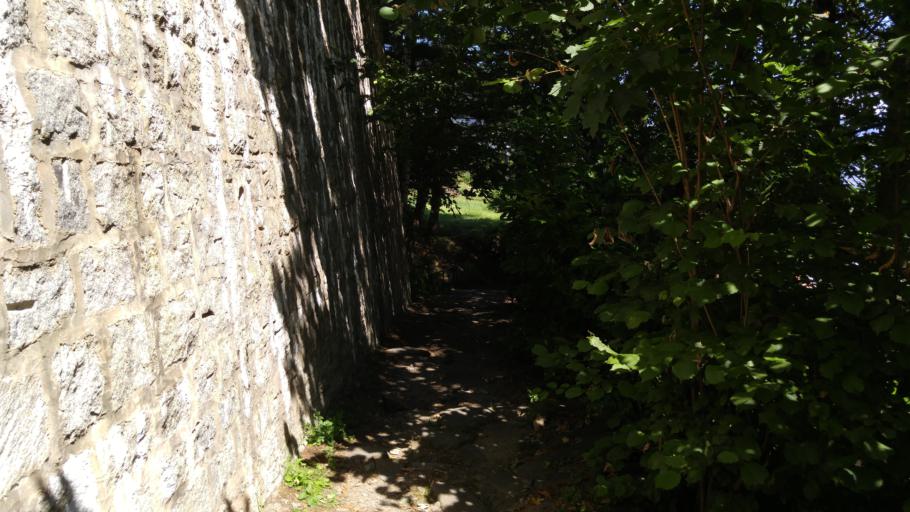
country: IT
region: Piedmont
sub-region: Provincia Verbano-Cusio-Ossola
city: Cannobio
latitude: 46.0727
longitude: 8.6872
